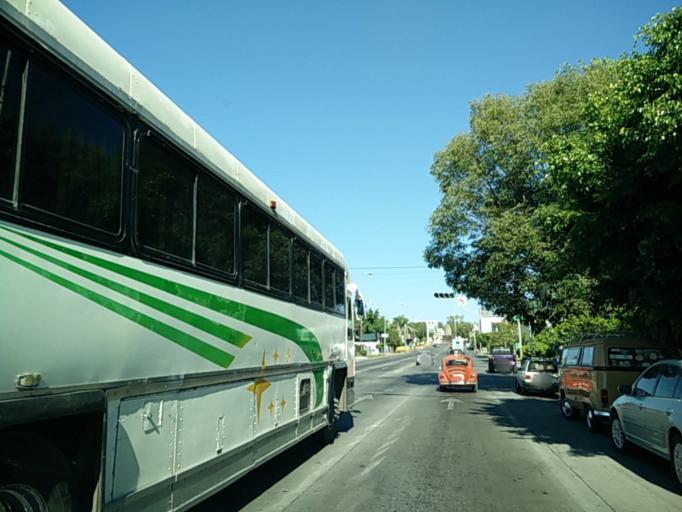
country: MX
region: Jalisco
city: Tlaquepaque
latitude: 20.6609
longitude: -103.3314
